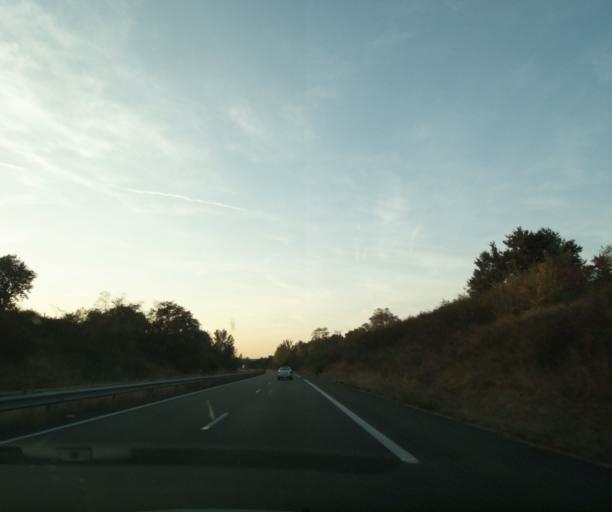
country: FR
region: Aquitaine
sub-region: Departement du Lot-et-Garonne
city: Sainte-Bazeille
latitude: 44.4580
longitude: 0.0832
